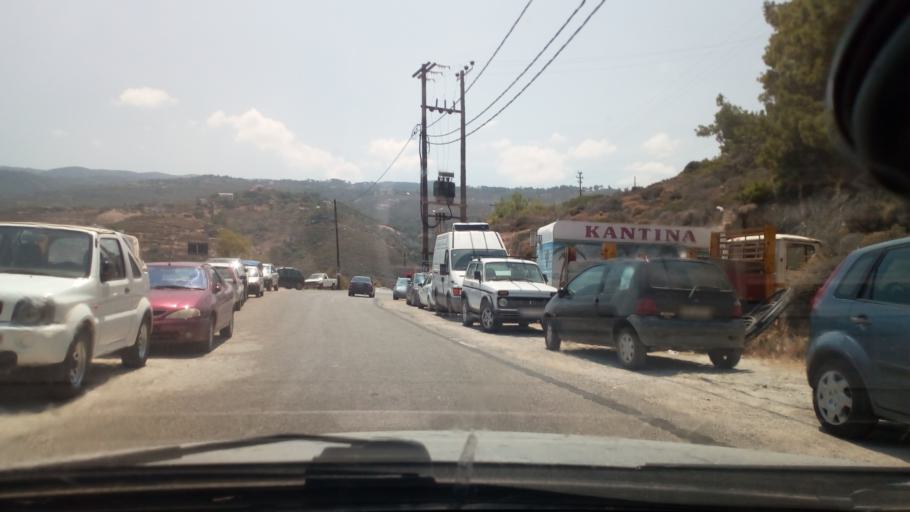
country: GR
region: North Aegean
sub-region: Nomos Samou
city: Agios Kirykos
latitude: 37.6326
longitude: 26.0881
